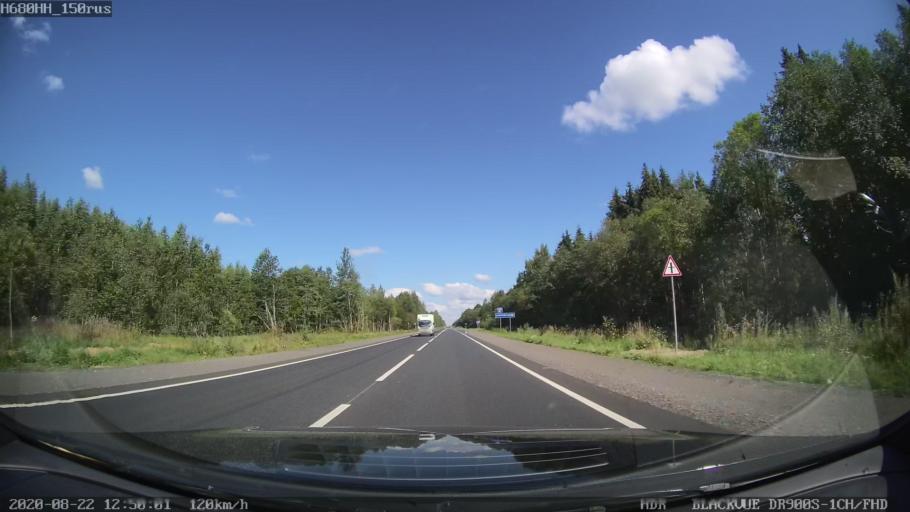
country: RU
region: Tverskaya
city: Rameshki
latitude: 57.4601
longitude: 36.2158
